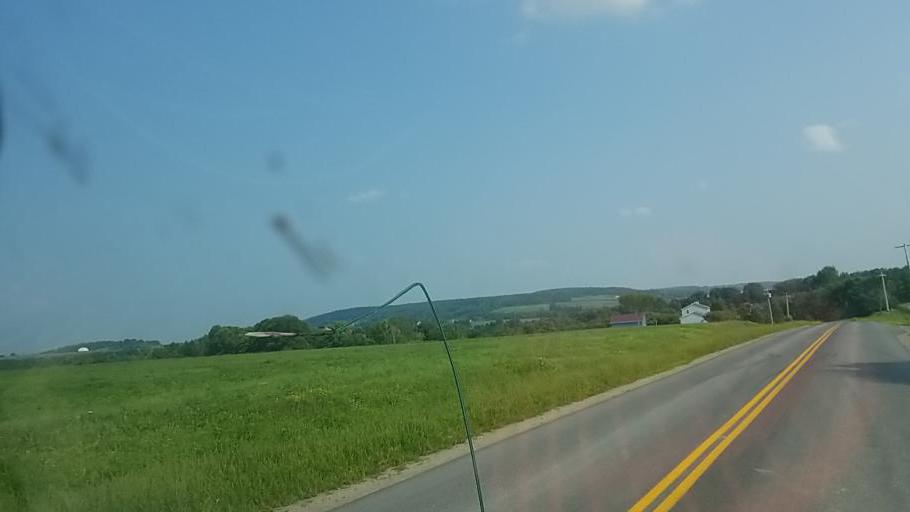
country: US
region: New York
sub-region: Montgomery County
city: Fonda
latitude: 42.9024
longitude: -74.3669
